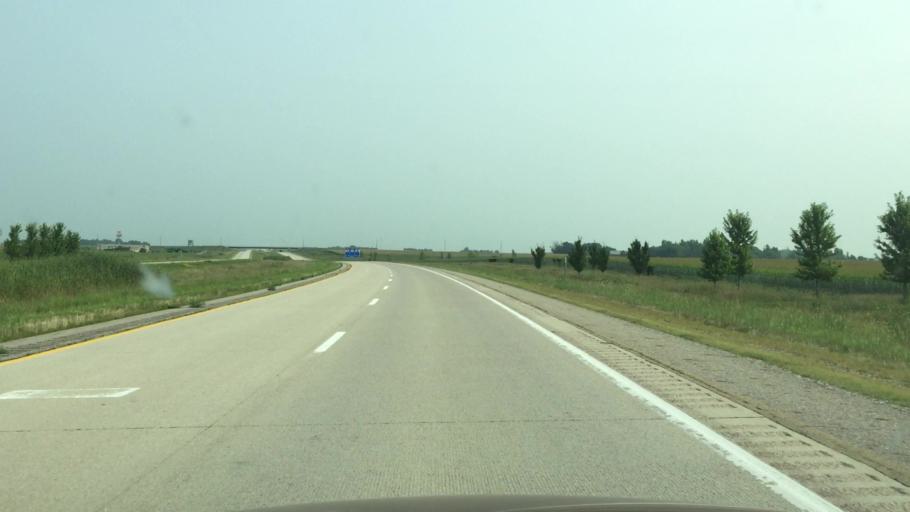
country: US
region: Iowa
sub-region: Osceola County
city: Sibley
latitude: 43.3939
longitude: -95.7178
